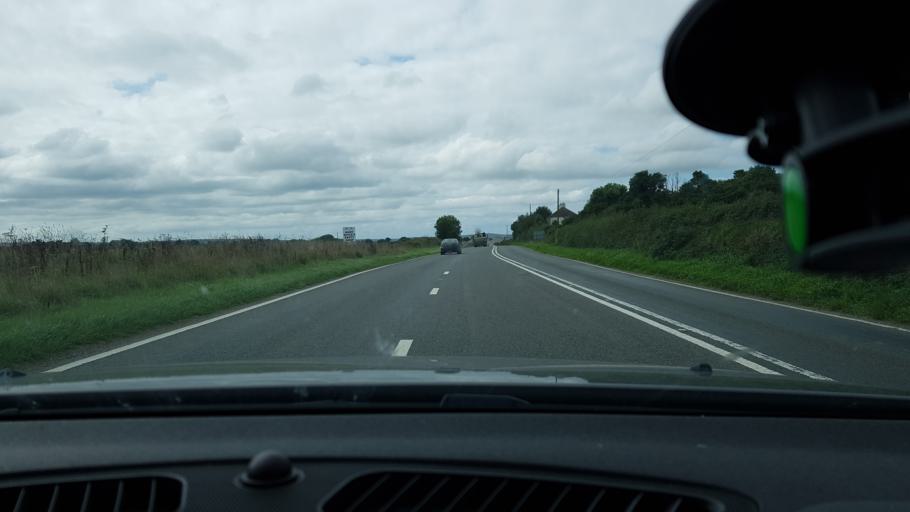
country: GB
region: England
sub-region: Cornwall
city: Helland
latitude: 50.5472
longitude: -4.7703
